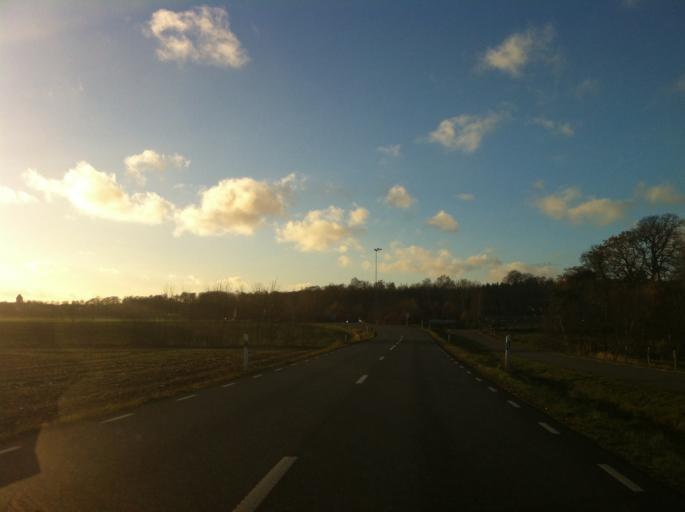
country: SE
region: Skane
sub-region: Hassleholms Kommun
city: Hastveda
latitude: 56.1996
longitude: 13.9120
